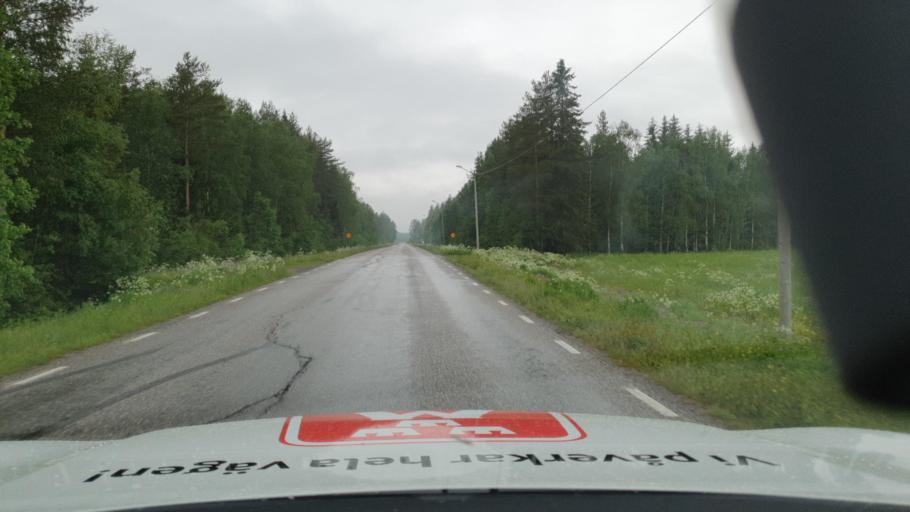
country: SE
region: Vaesterbotten
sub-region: Nordmalings Kommun
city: Nordmaling
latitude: 63.7923
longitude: 19.5435
